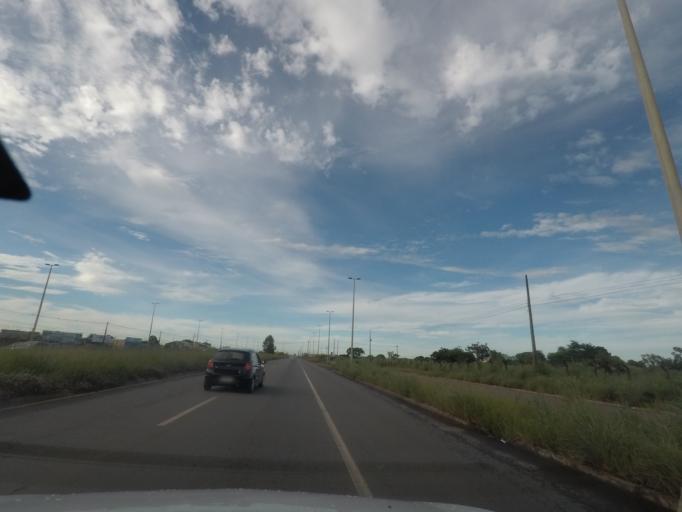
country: BR
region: Goias
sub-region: Aparecida De Goiania
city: Aparecida de Goiania
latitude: -16.7749
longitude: -49.3522
